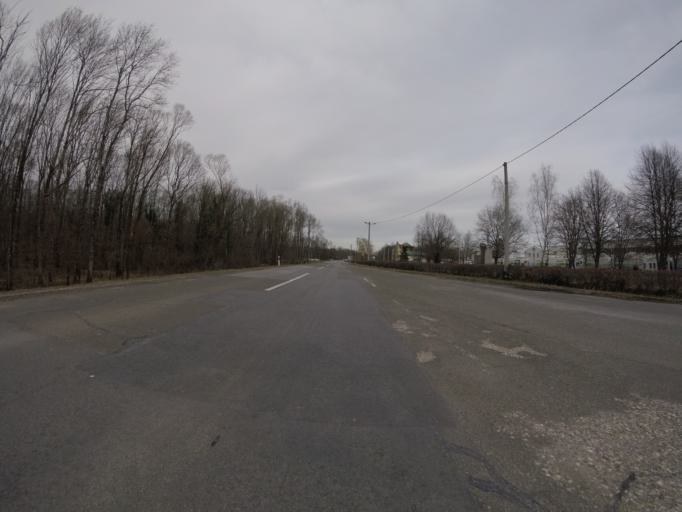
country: HR
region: Grad Zagreb
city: Horvati
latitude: 45.5511
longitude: 15.8581
